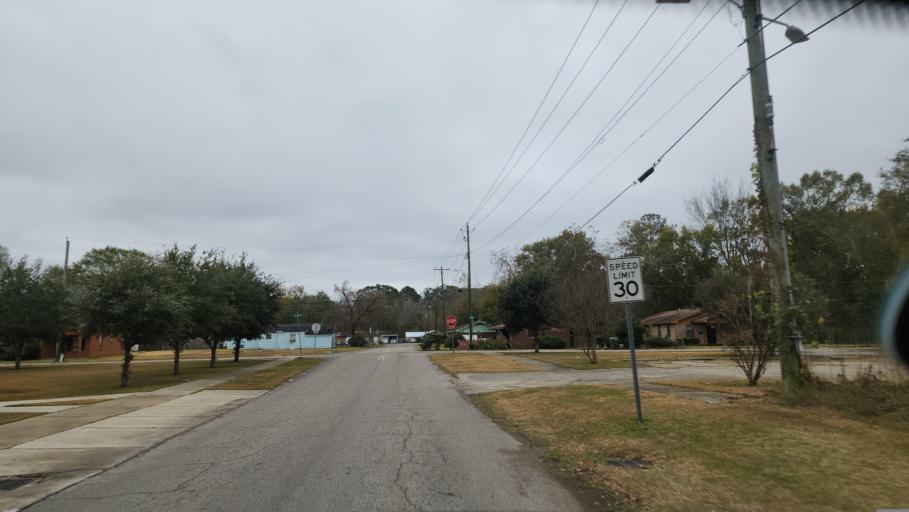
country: US
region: Mississippi
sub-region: Forrest County
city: Hattiesburg
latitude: 31.3119
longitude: -89.2946
